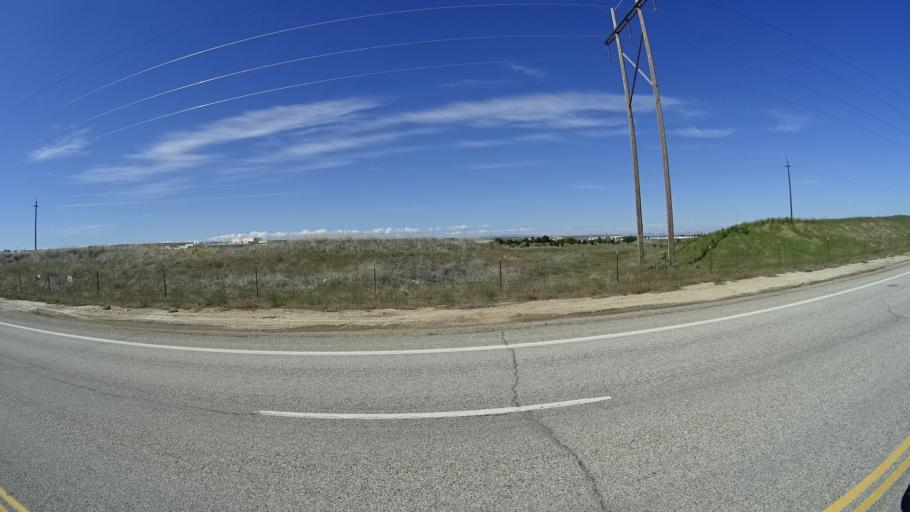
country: US
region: Idaho
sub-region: Ada County
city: Boise
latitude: 43.5360
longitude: -116.1442
